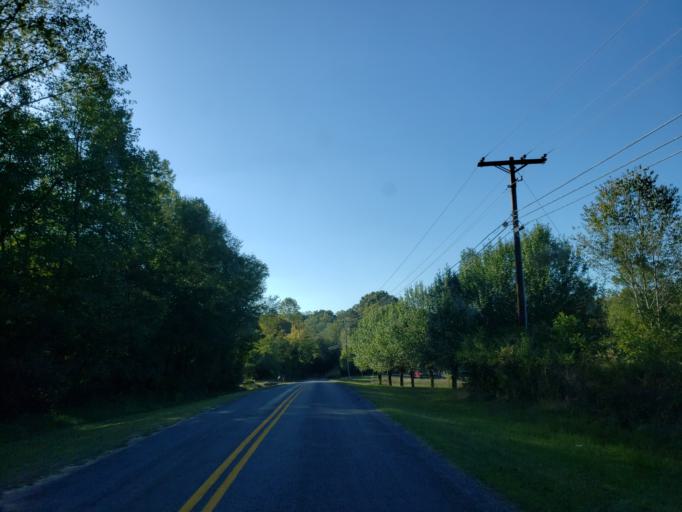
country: US
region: Georgia
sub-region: Pickens County
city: Nelson
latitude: 34.3862
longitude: -84.4060
